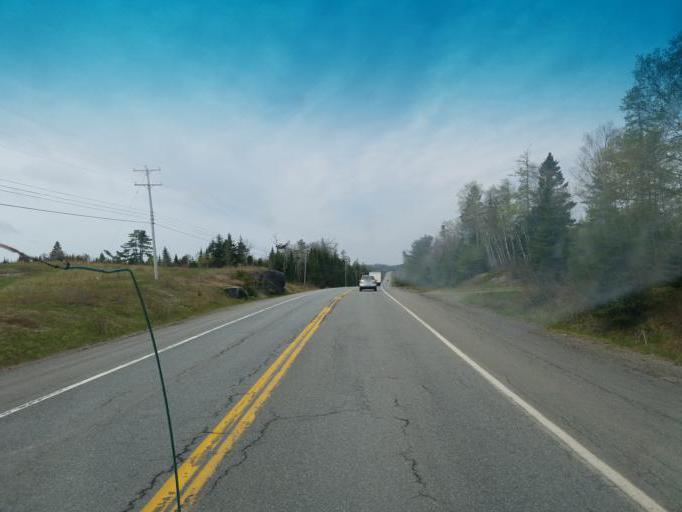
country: US
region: Maine
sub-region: Washington County
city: East Machias
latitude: 44.7551
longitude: -67.2353
